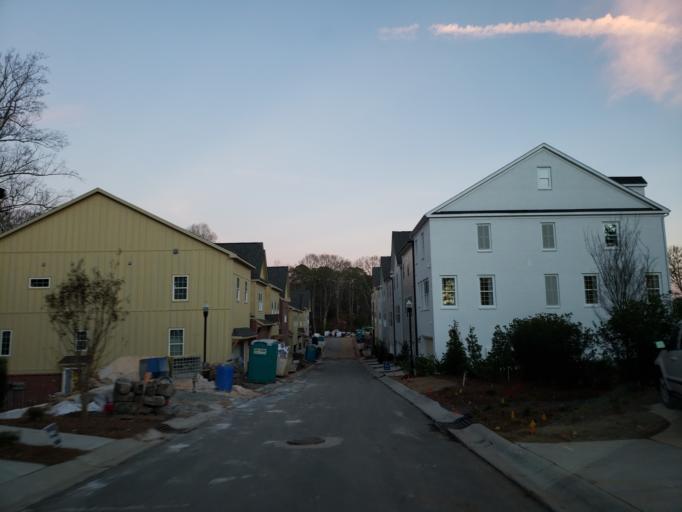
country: US
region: Georgia
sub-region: Fulton County
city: Alpharetta
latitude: 34.0722
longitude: -84.2886
